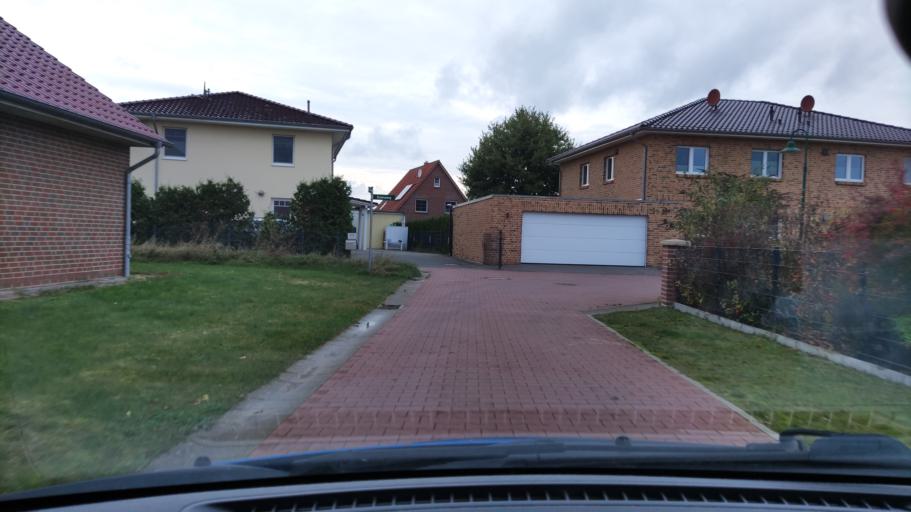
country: DE
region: Schleswig-Holstein
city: Escheburg
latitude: 53.4238
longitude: 10.3166
